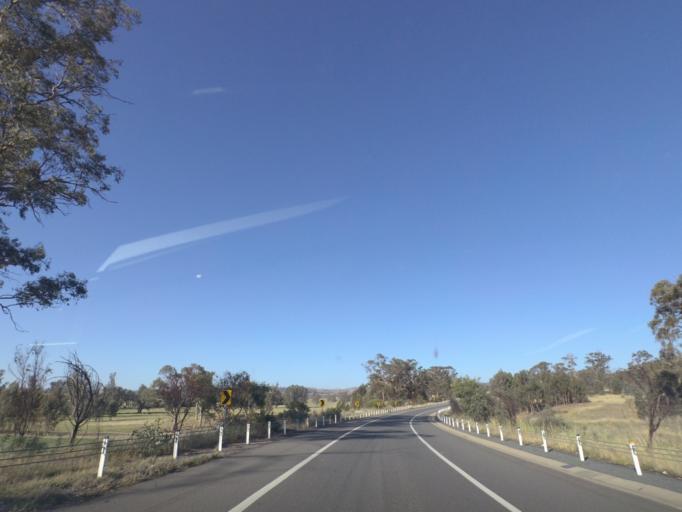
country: AU
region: New South Wales
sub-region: Wagga Wagga
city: Forest Hill
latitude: -35.2599
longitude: 147.7462
